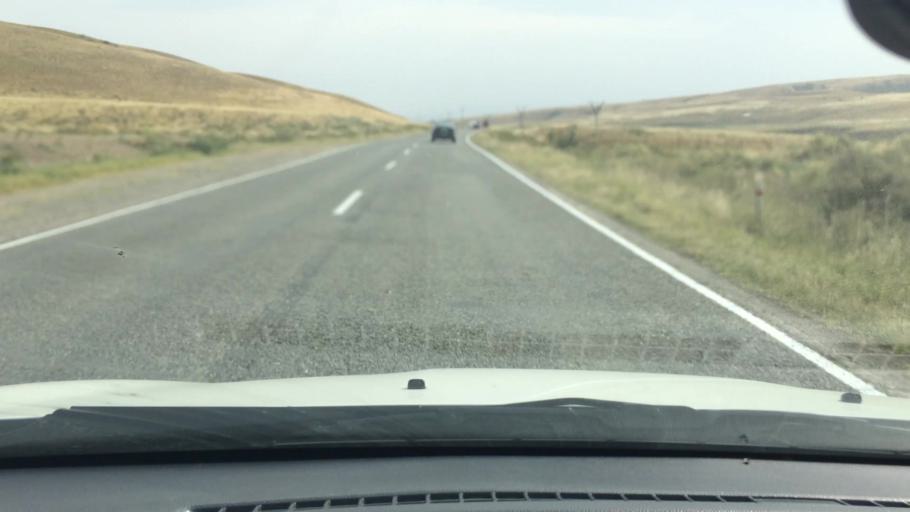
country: GE
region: Kvemo Kartli
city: Rust'avi
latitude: 41.5050
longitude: 44.9536
